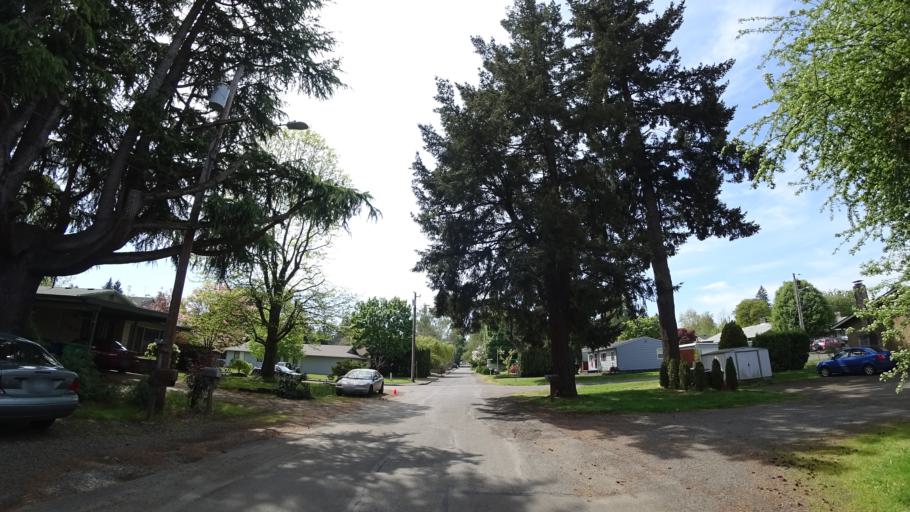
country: US
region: Oregon
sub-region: Clackamas County
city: Milwaukie
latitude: 45.4476
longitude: -122.6144
